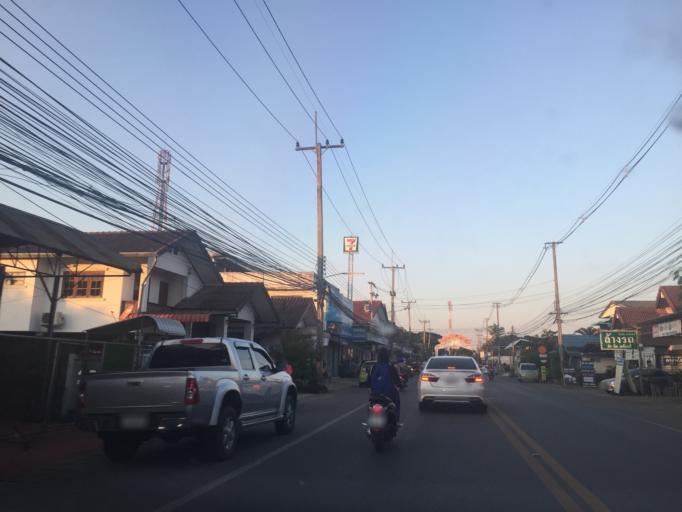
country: TH
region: Lamphun
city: Lamphun
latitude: 18.6076
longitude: 99.0246
